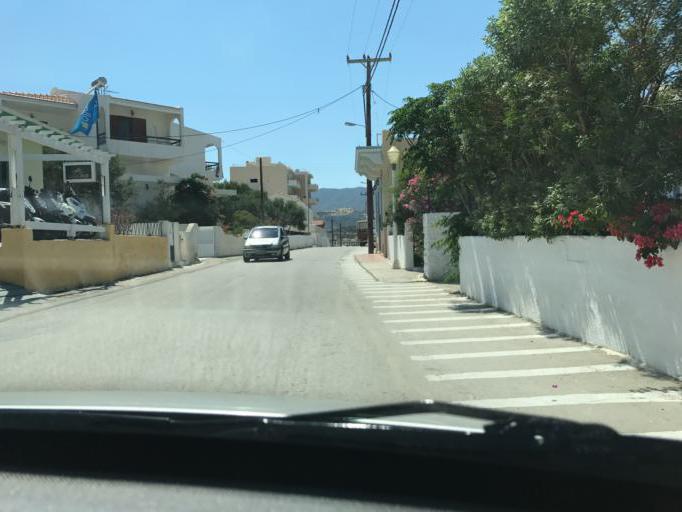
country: GR
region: South Aegean
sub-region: Nomos Dodekanisou
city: Karpathos
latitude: 35.5073
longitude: 27.2088
